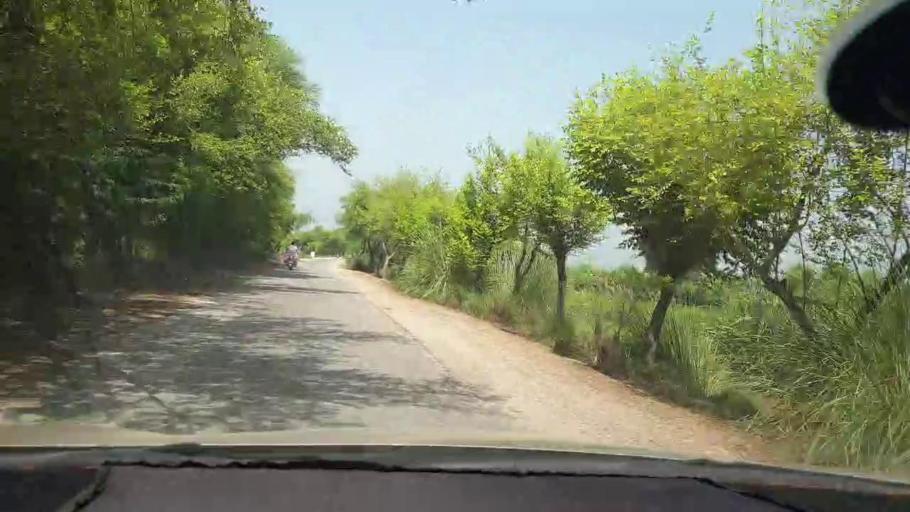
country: PK
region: Sindh
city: Kambar
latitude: 27.6418
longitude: 67.9737
